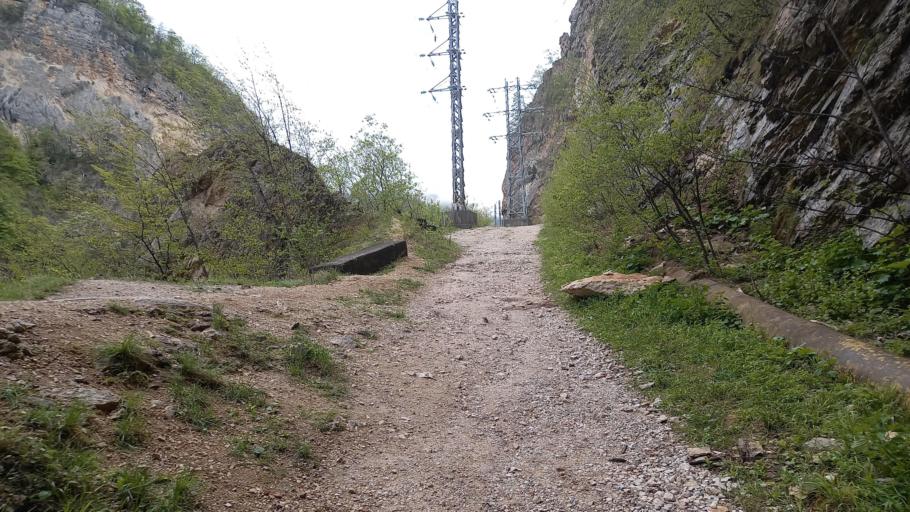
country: RU
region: Kabardino-Balkariya
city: Verkhnyaya Balkariya
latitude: 43.1882
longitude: 43.5162
